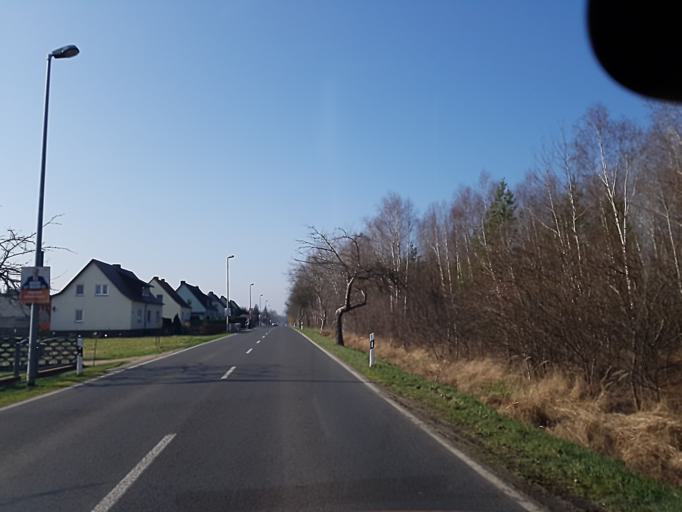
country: DE
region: Brandenburg
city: Forst
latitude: 51.6947
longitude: 14.6043
